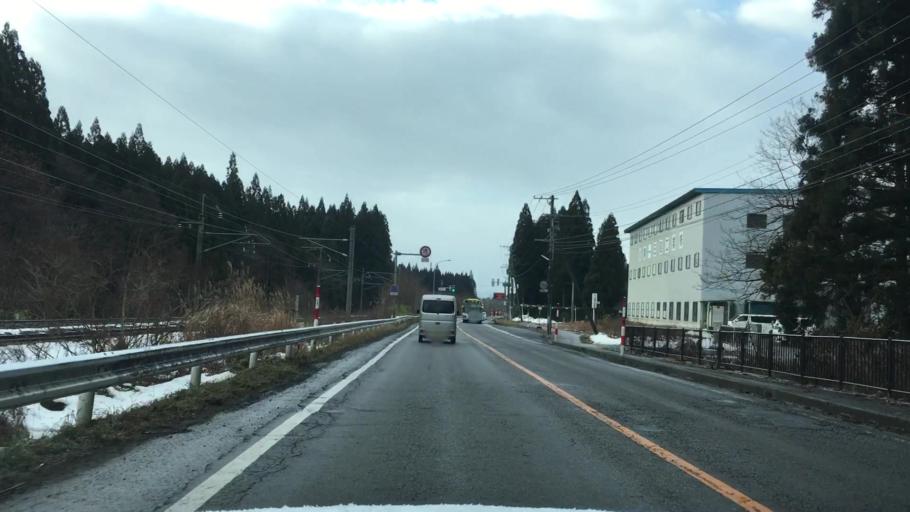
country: JP
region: Akita
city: Odate
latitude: 40.3239
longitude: 140.5818
